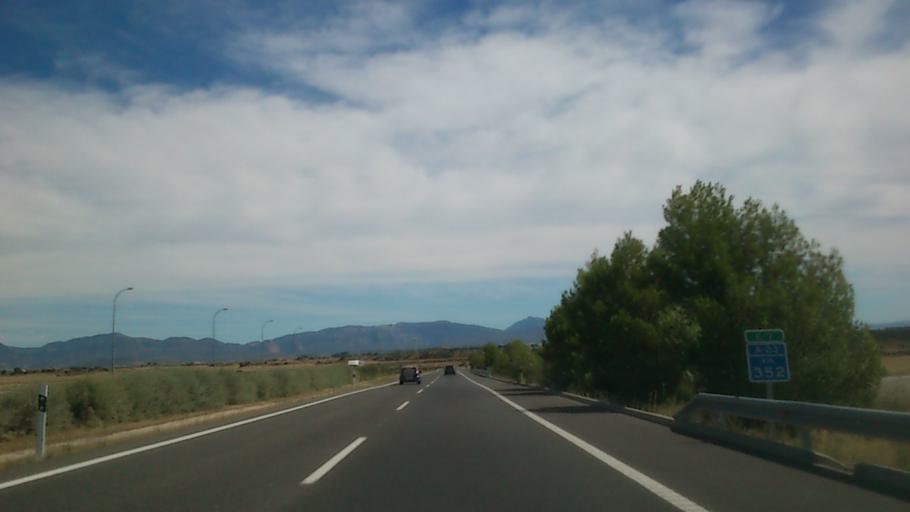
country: ES
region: Aragon
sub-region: Provincia de Huesca
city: Alerre
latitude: 42.0917
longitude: -0.4776
